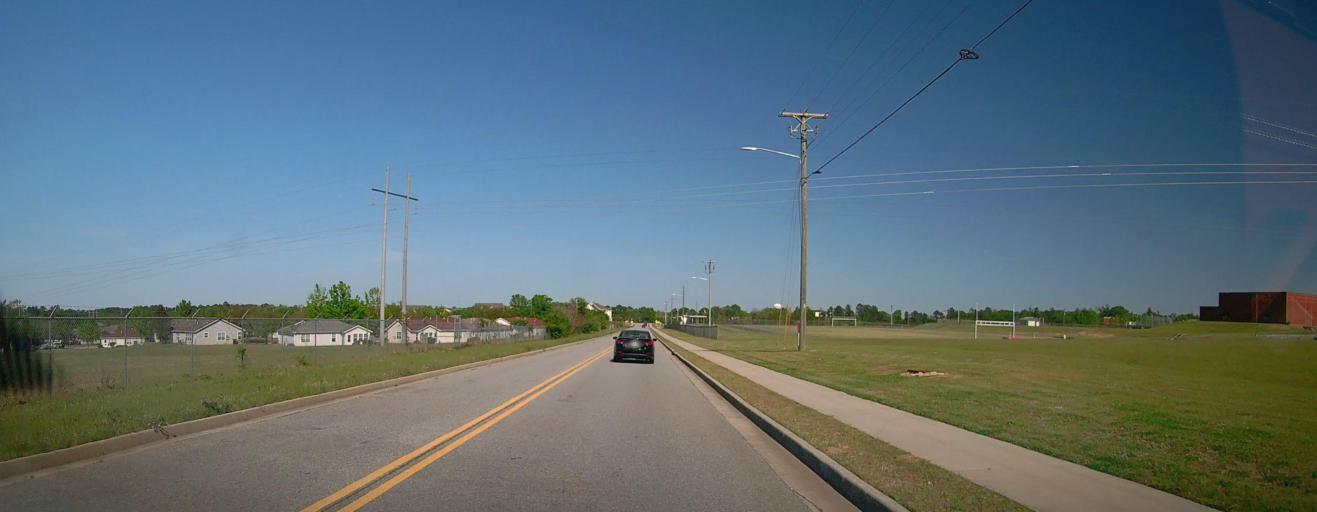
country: US
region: Georgia
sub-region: Houston County
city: Robins Air Force Base
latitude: 32.6017
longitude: -83.6022
